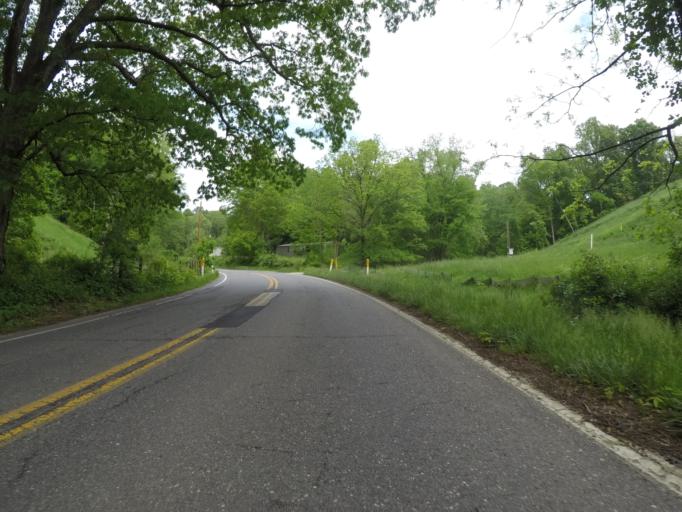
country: US
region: West Virginia
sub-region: Wayne County
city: Ceredo
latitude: 38.3546
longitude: -82.5475
